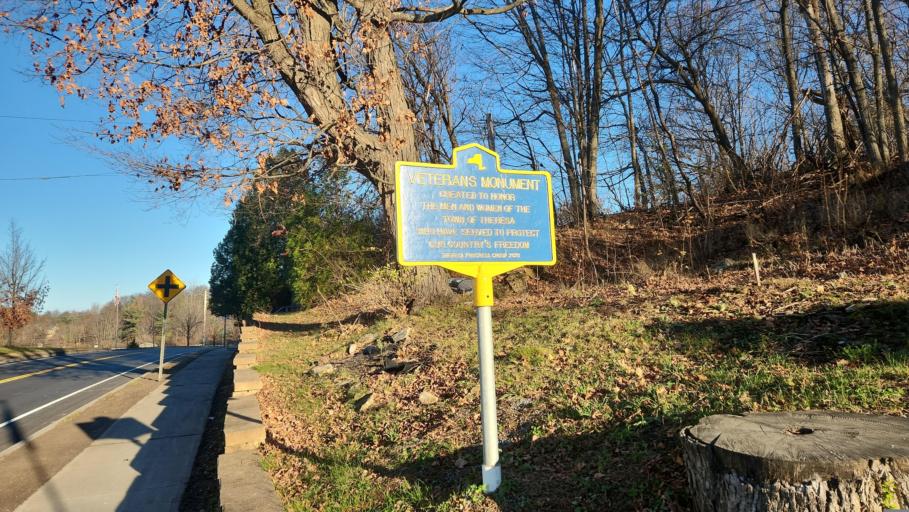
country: US
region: New York
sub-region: Jefferson County
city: Philadelphia
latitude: 44.2161
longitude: -75.7960
